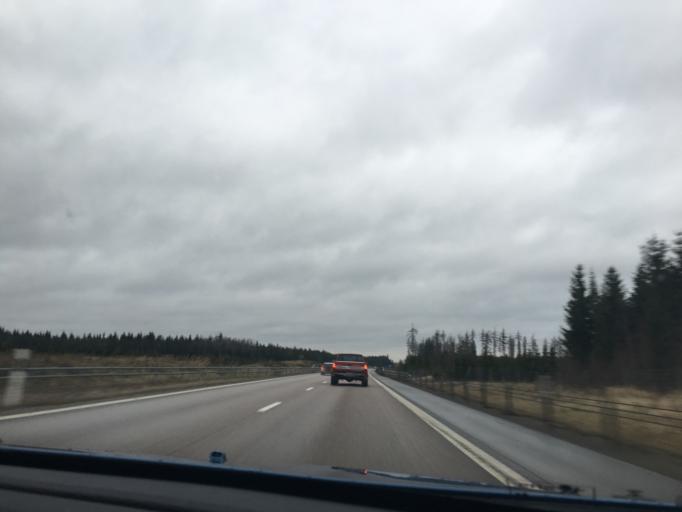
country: SE
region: Uppsala
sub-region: Tierps Kommun
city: Tierp
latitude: 60.4199
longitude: 17.4447
